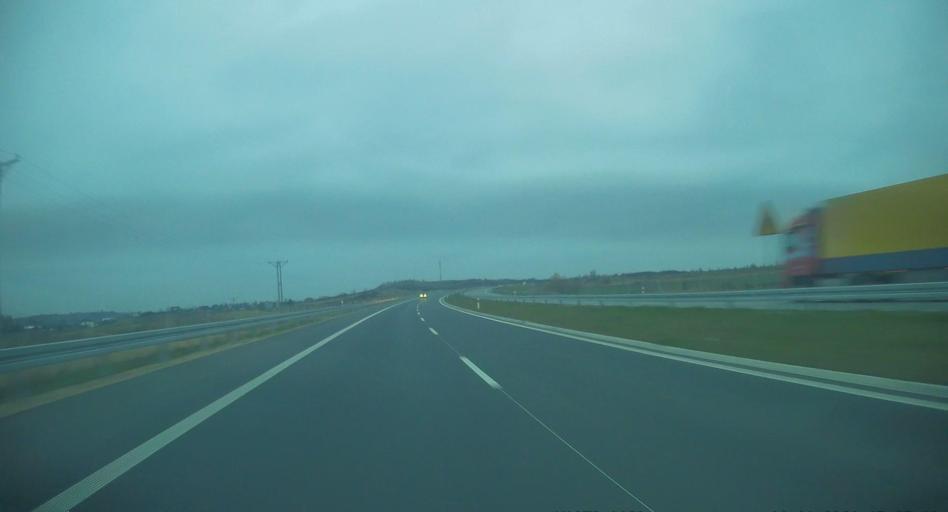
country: PL
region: Silesian Voivodeship
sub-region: Powiat bedzinski
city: Mierzecice
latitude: 50.4248
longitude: 19.1651
